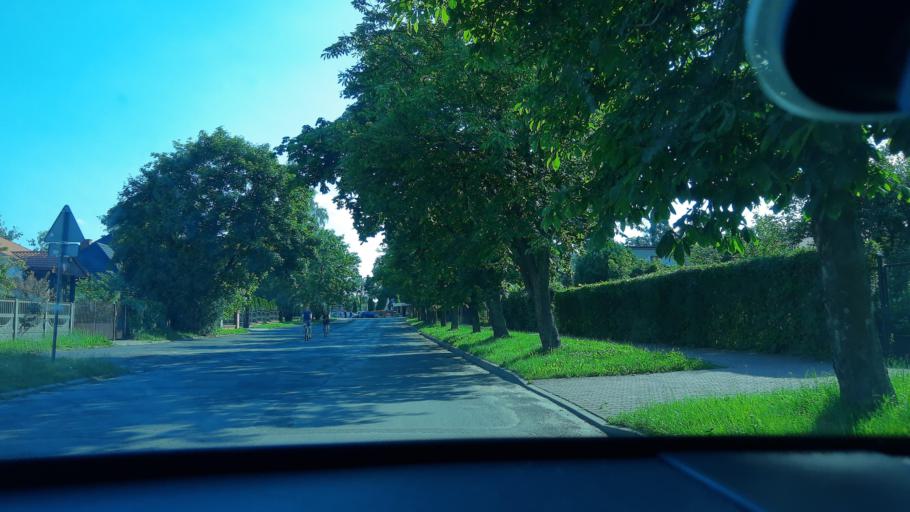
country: PL
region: Lodz Voivodeship
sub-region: Powiat sieradzki
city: Sieradz
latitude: 51.6003
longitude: 18.7300
